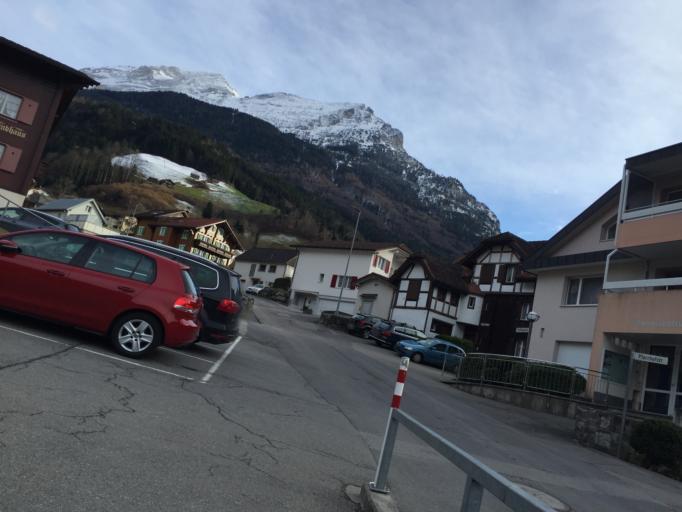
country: CH
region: Uri
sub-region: Uri
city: Schattdorf
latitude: 46.8633
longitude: 8.6559
